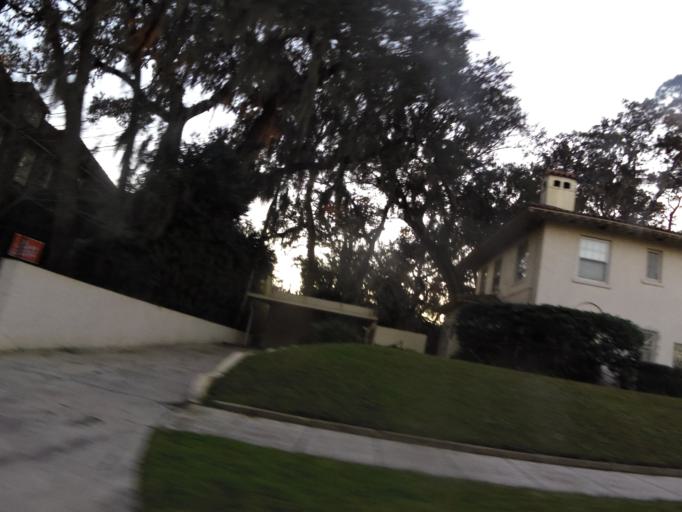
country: US
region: Florida
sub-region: Duval County
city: Jacksonville
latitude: 30.2981
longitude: -81.7018
